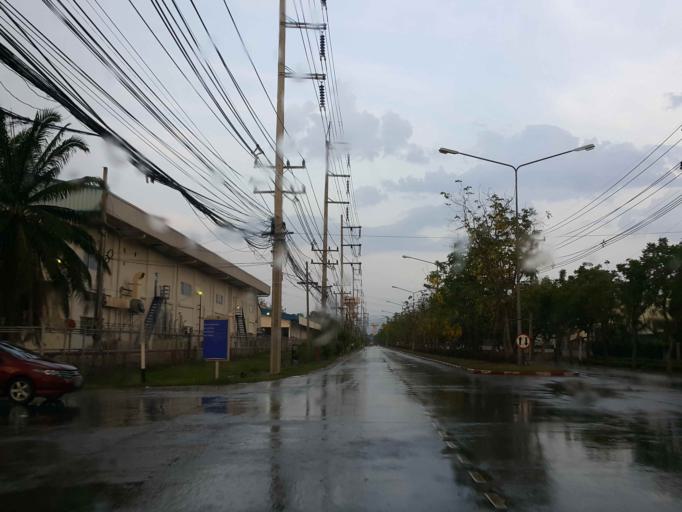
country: TH
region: Lamphun
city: Lamphun
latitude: 18.5906
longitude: 99.0468
